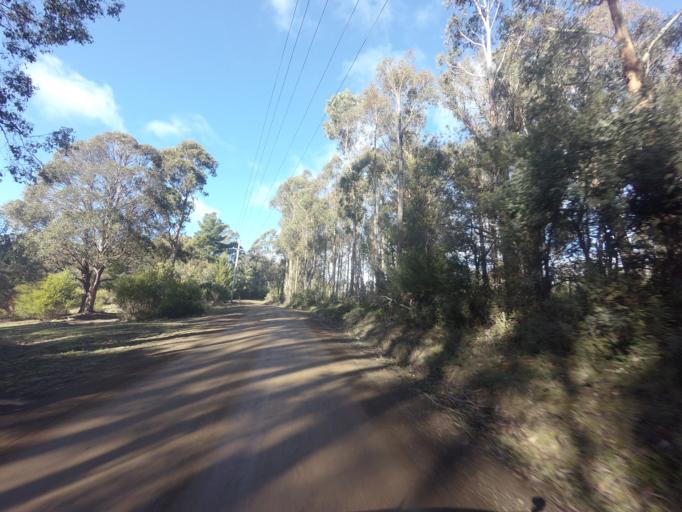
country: AU
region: Tasmania
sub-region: Derwent Valley
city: New Norfolk
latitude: -42.8365
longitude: 147.1329
